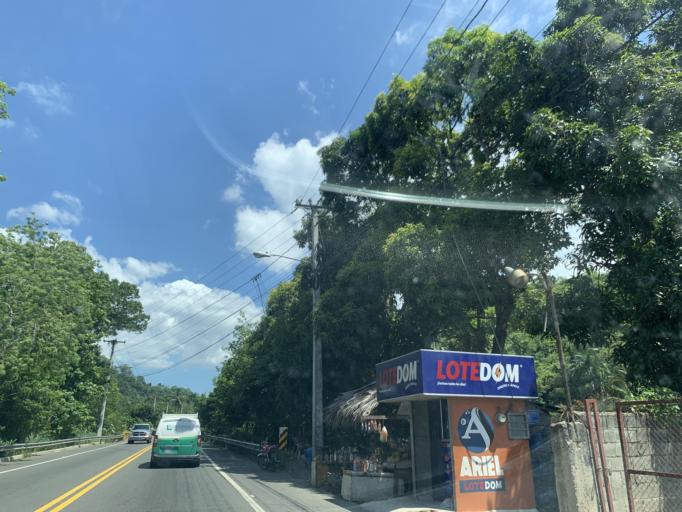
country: DO
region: Puerto Plata
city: Altamira
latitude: 19.6942
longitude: -70.8406
